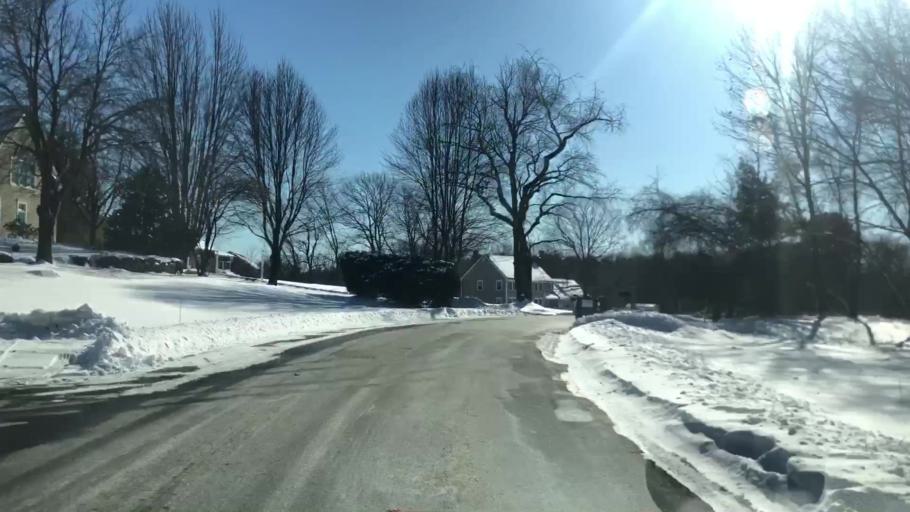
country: US
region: New Hampshire
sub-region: Hillsborough County
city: Bedford
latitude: 42.9435
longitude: -71.5421
